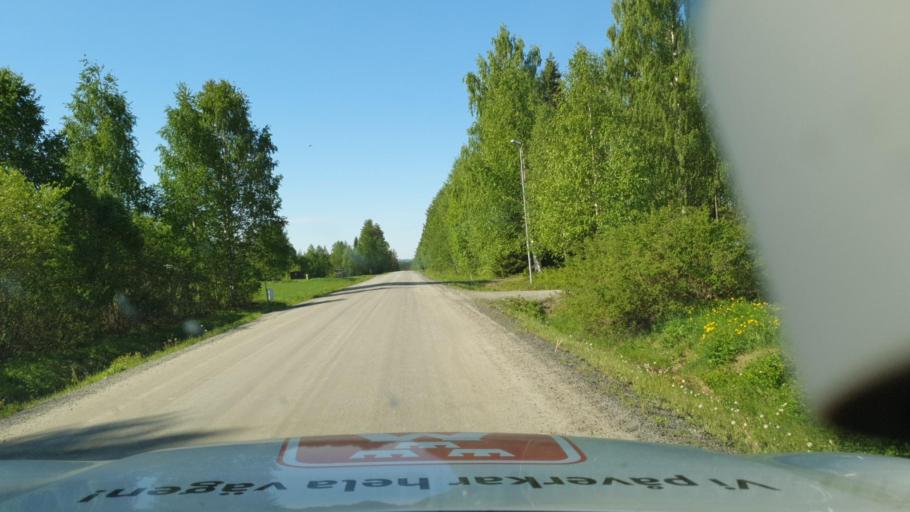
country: SE
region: Vaesterbotten
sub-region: Vannas Kommun
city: Vaennaes
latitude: 64.0148
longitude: 19.7437
